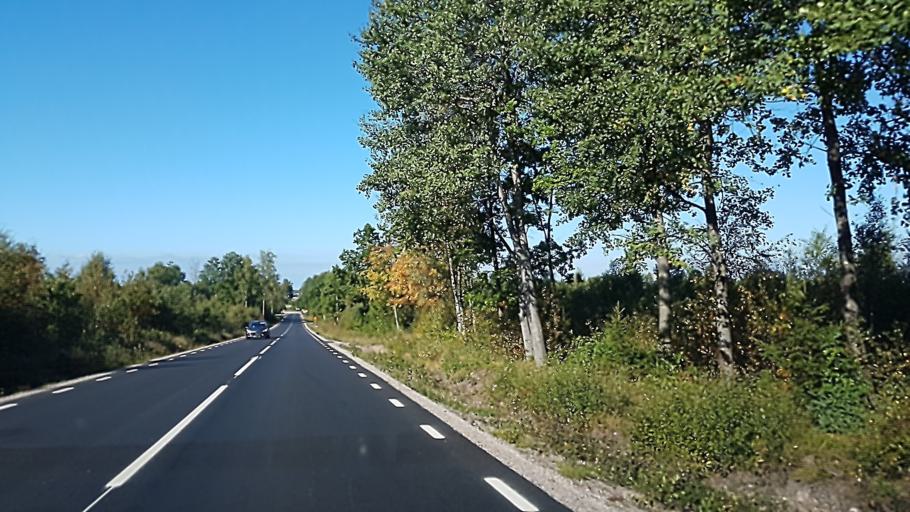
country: SE
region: Kronoberg
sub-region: Ljungby Kommun
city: Ljungby
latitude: 56.8275
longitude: 13.9794
